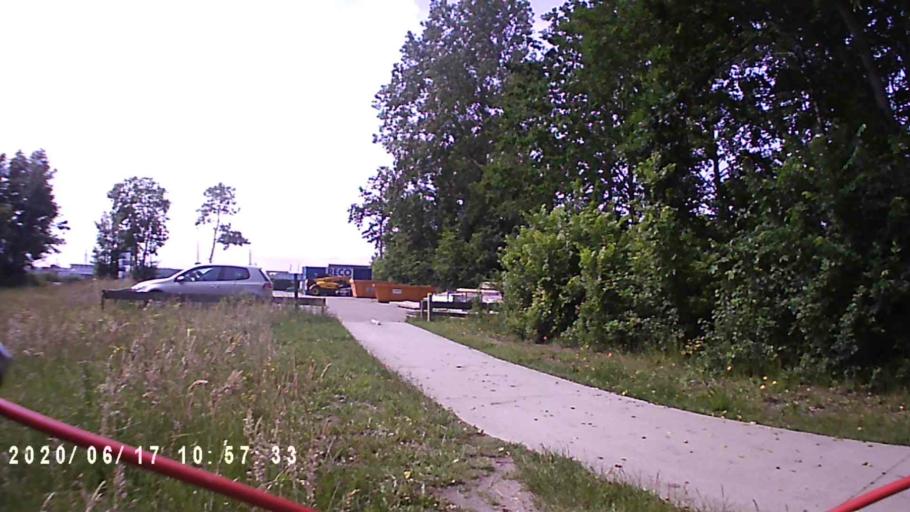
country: NL
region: Friesland
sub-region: Gemeente Dongeradeel
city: Anjum
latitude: 53.4058
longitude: 6.2081
